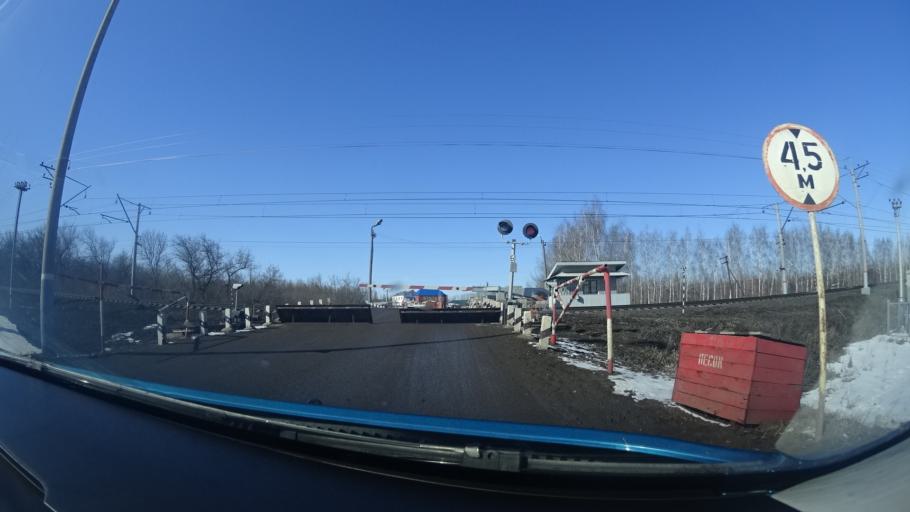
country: RU
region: Bashkortostan
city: Chishmy
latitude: 54.5790
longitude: 55.3708
